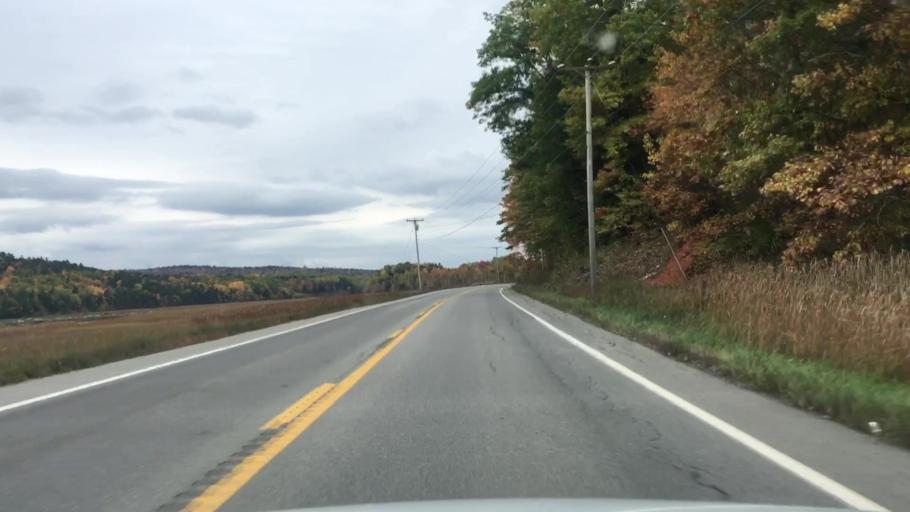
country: US
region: Maine
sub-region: Waldo County
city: Frankfort
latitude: 44.5866
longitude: -68.8641
